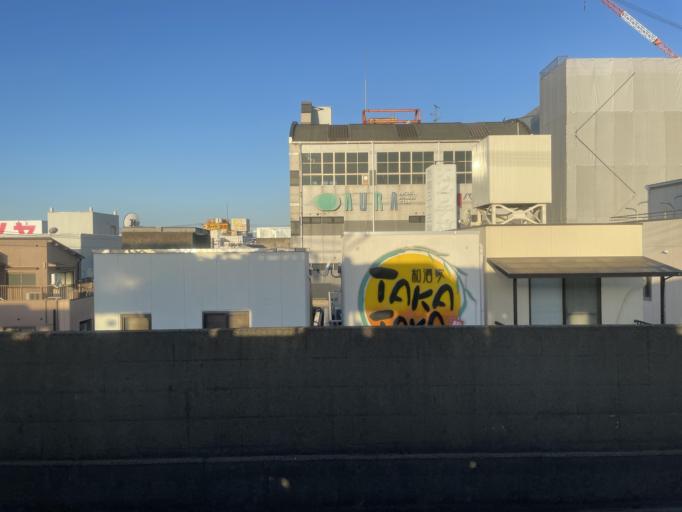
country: JP
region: Osaka
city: Matsubara
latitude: 34.6182
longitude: 135.5329
